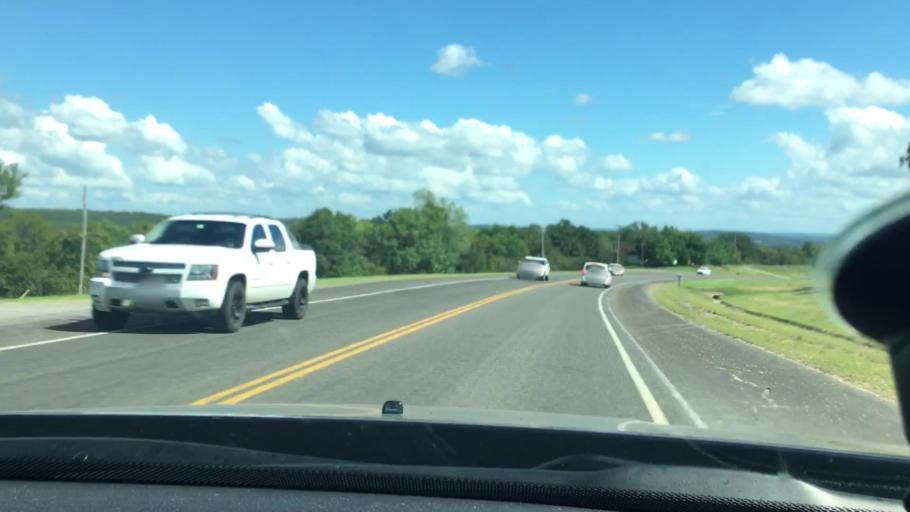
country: US
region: Oklahoma
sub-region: Sequoyah County
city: Vian
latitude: 35.5517
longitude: -94.9718
